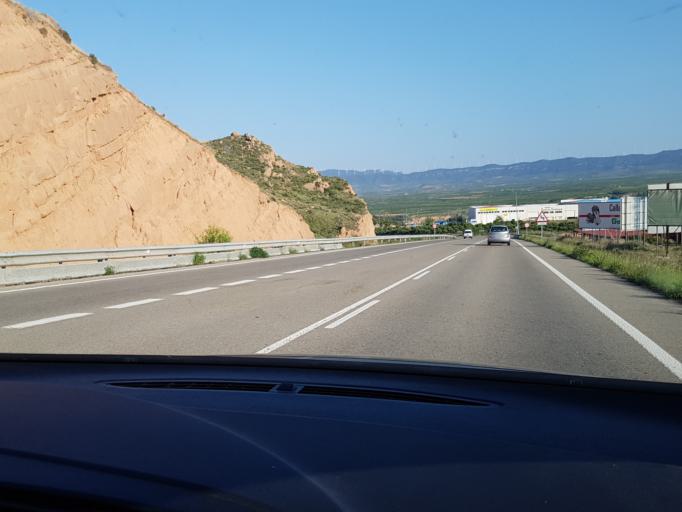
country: ES
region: La Rioja
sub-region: Provincia de La Rioja
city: Arnedo
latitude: 42.2382
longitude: -2.0859
